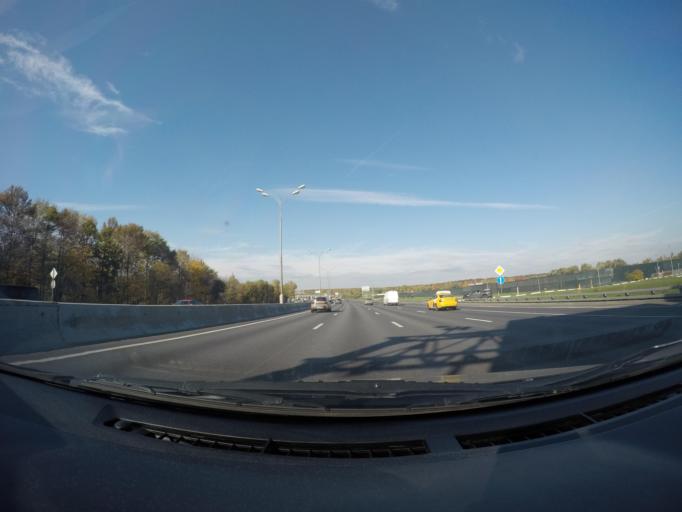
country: RU
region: Moscow
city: Gol'yanovo
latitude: 55.8259
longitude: 37.8340
